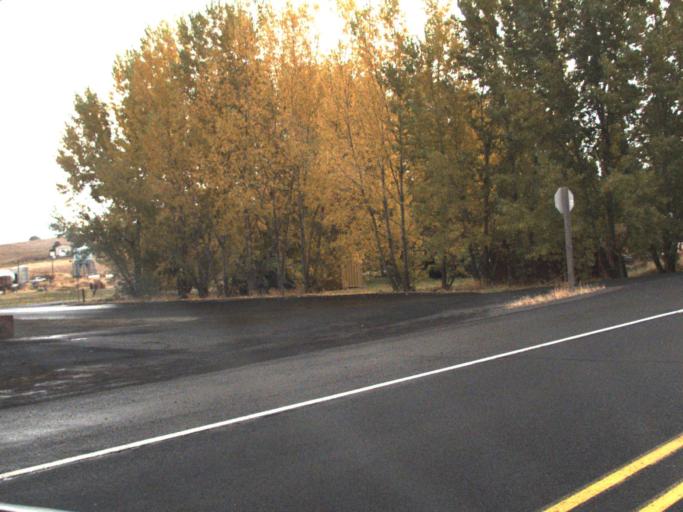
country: US
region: Washington
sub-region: Asotin County
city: Clarkston
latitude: 46.5422
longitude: -117.0884
